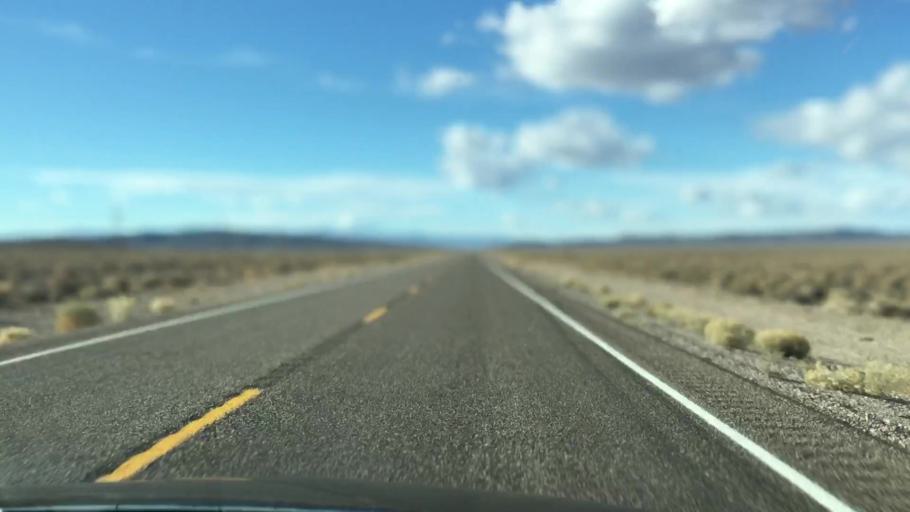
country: US
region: Nevada
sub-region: Nye County
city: Beatty
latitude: 37.1291
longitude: -116.8387
